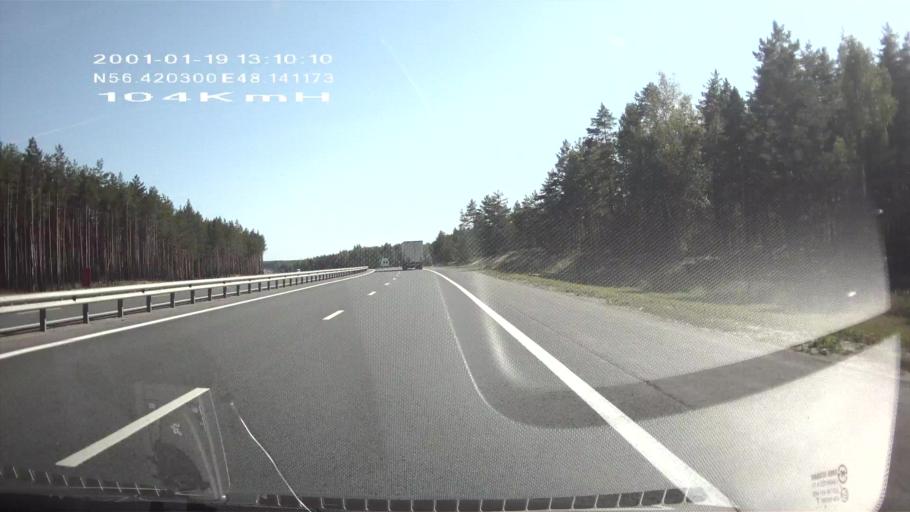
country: RU
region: Mariy-El
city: Surok
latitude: 56.4200
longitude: 48.1413
